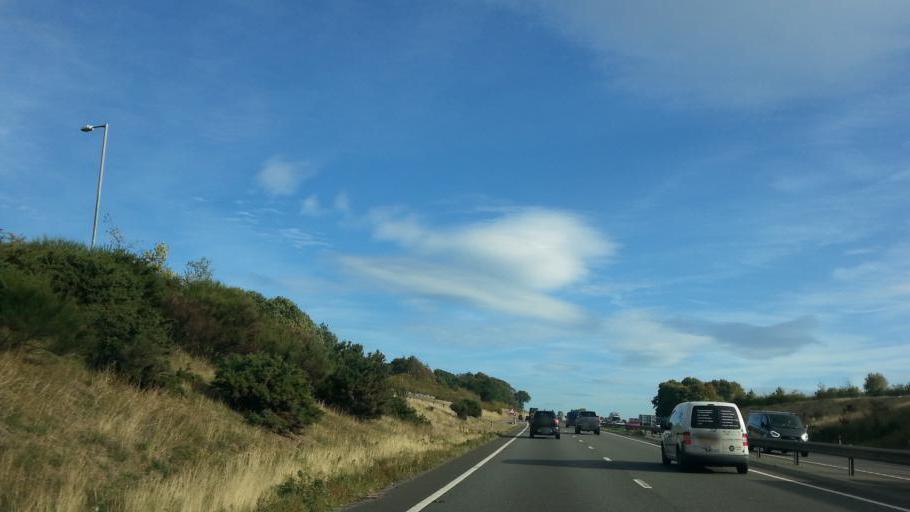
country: GB
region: England
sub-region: Nottinghamshire
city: Bircotes
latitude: 53.3880
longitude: -1.0634
